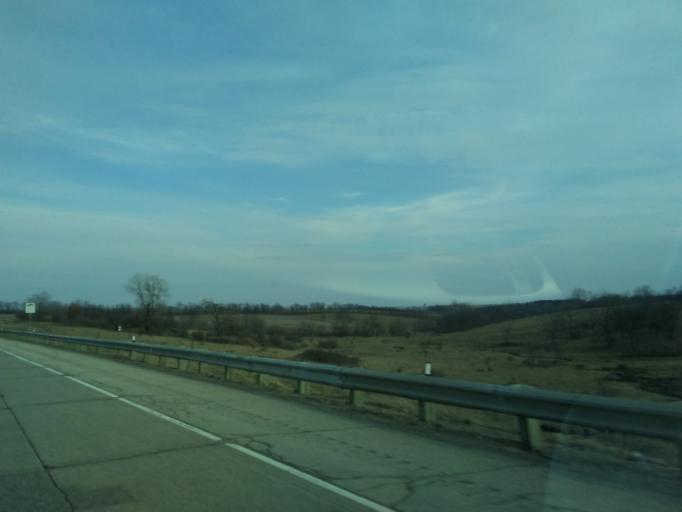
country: US
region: Wisconsin
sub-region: Iowa County
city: Dodgeville
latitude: 42.9673
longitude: -90.0921
